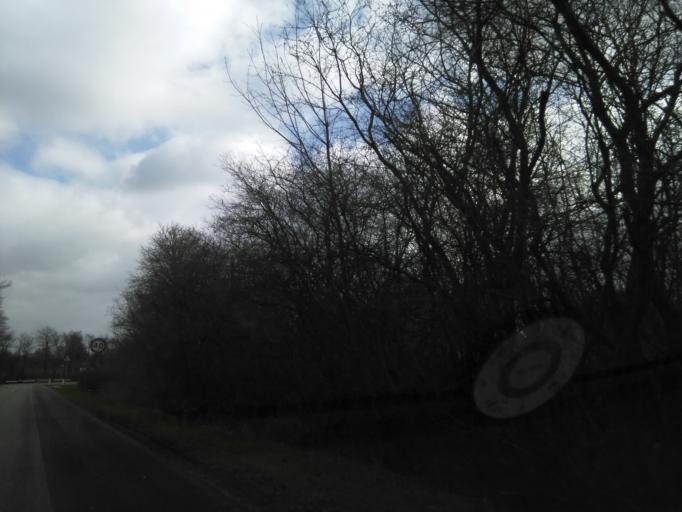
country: DK
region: Central Jutland
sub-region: Arhus Kommune
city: Beder
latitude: 56.0416
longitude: 10.2618
